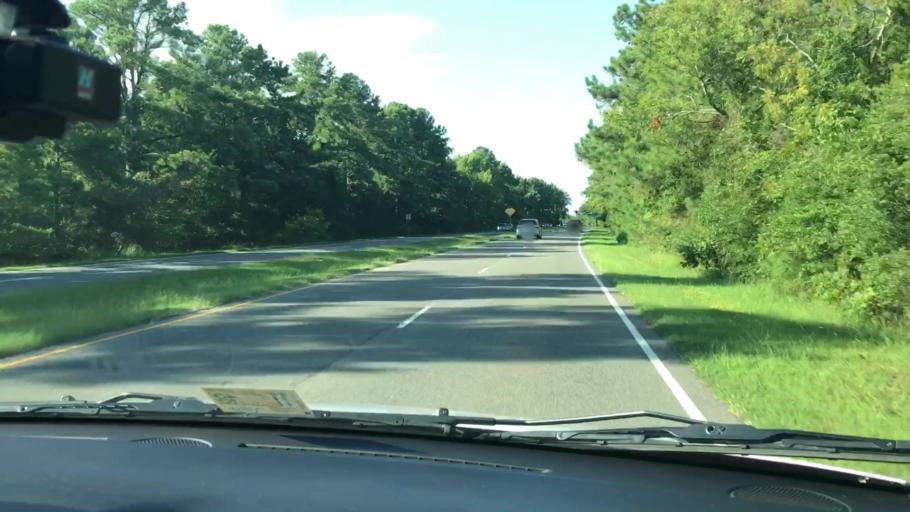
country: US
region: Virginia
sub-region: City of Hampton
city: Hampton
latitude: 37.0568
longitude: -76.3659
